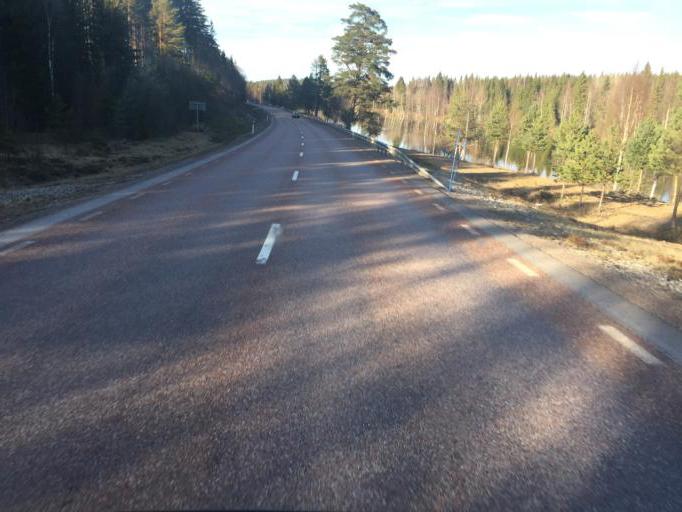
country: SE
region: Dalarna
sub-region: Gagnefs Kommun
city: Mockfjard
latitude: 60.4651
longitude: 14.7625
